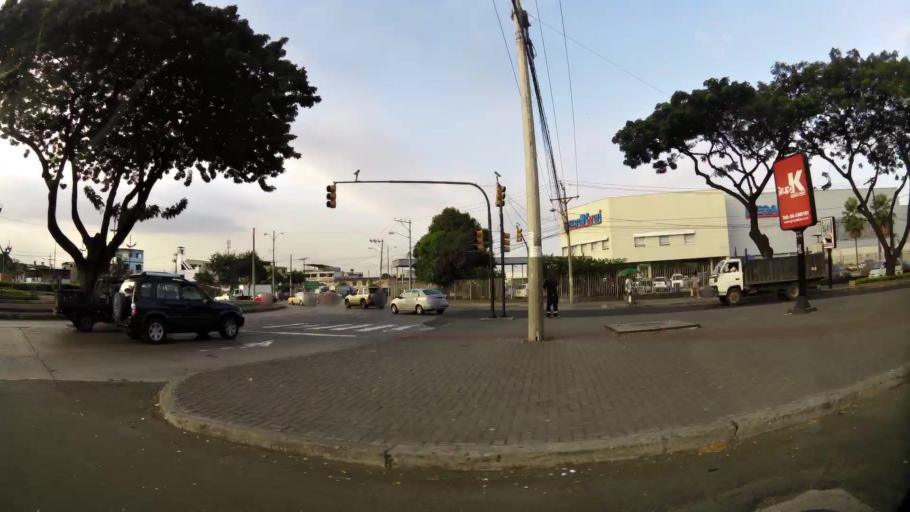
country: EC
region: Guayas
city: Eloy Alfaro
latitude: -2.1422
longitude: -79.8887
